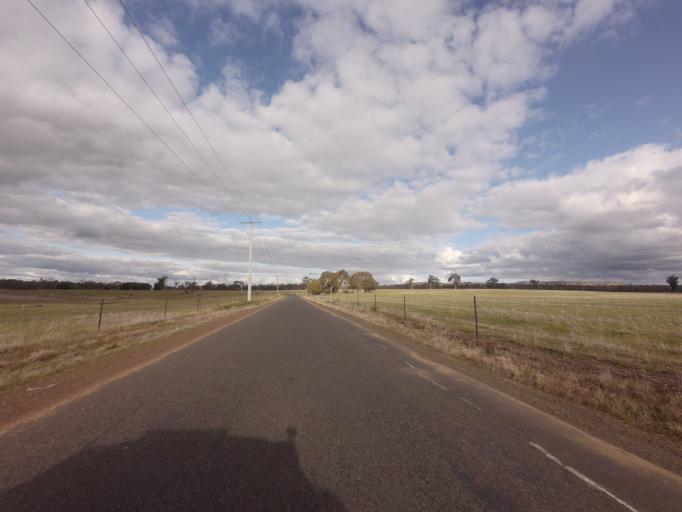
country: AU
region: Tasmania
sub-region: Northern Midlands
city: Evandale
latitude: -41.8644
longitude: 147.2674
